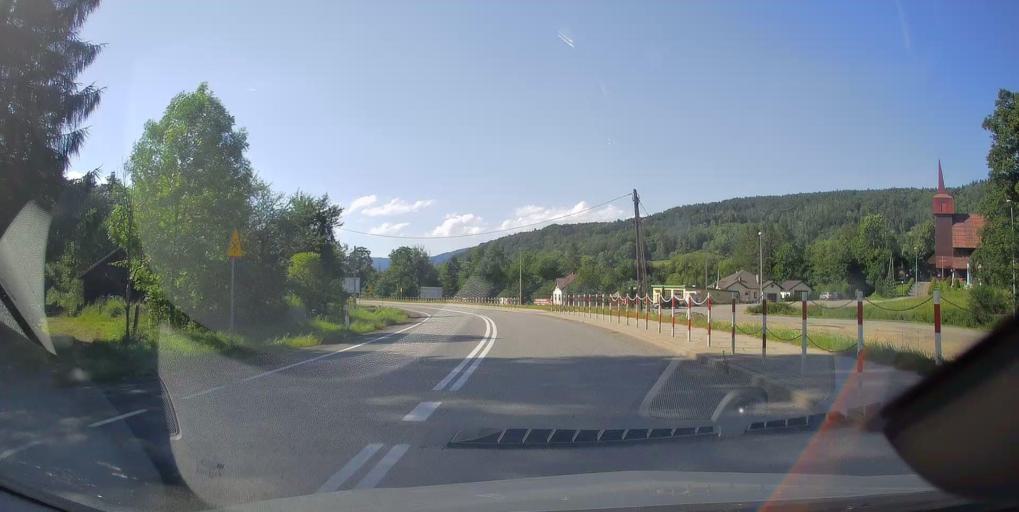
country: PL
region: Lesser Poland Voivodeship
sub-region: Powiat nowosadecki
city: Labowa
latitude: 49.4952
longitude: 20.9069
